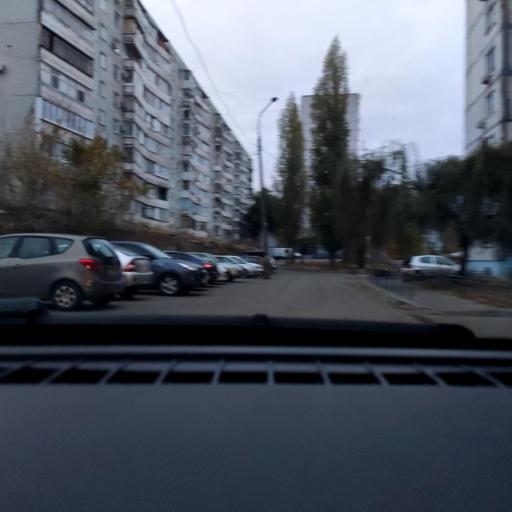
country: RU
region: Voronezj
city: Voronezh
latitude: 51.6367
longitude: 39.2323
